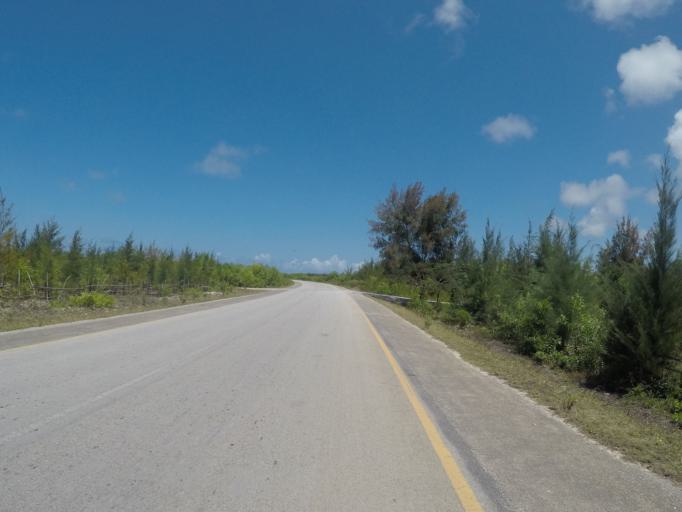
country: TZ
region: Zanzibar Central/South
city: Nganane
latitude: -6.3928
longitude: 39.5586
